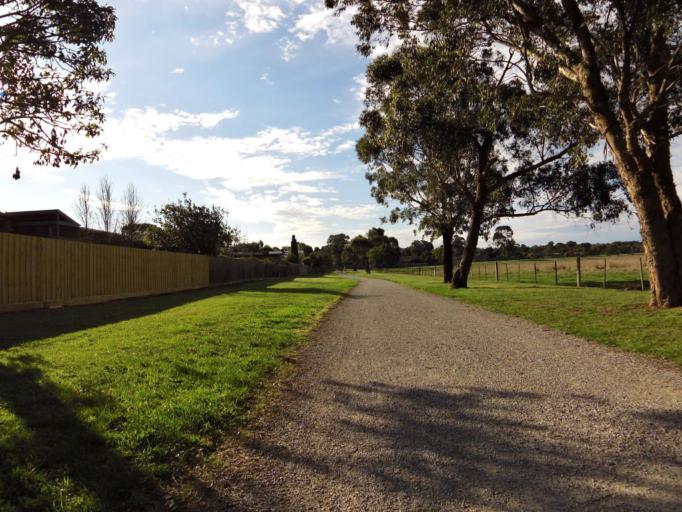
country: AU
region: Victoria
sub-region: Whitehorse
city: Vermont South
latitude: -37.8715
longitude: 145.1882
